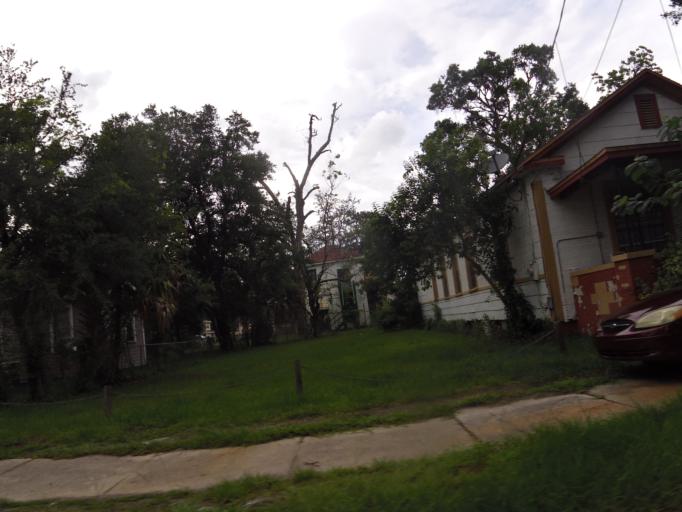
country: US
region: Florida
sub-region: Duval County
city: Jacksonville
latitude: 30.3435
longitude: -81.6749
